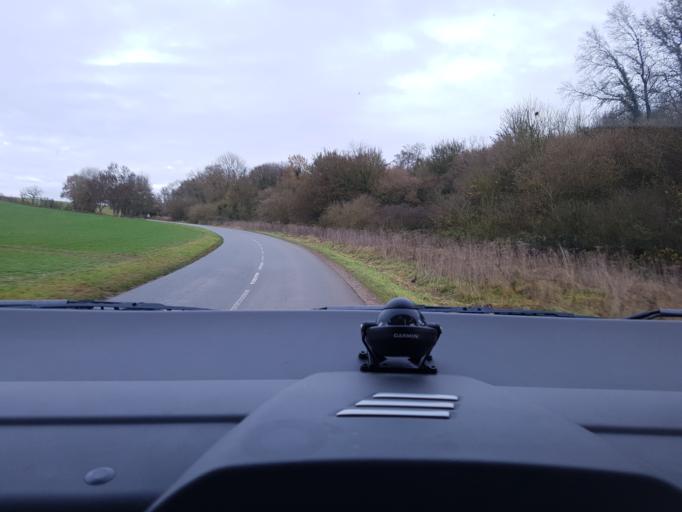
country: FR
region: Picardie
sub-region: Departement de l'Oise
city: Songeons
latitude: 49.5695
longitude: 1.8597
